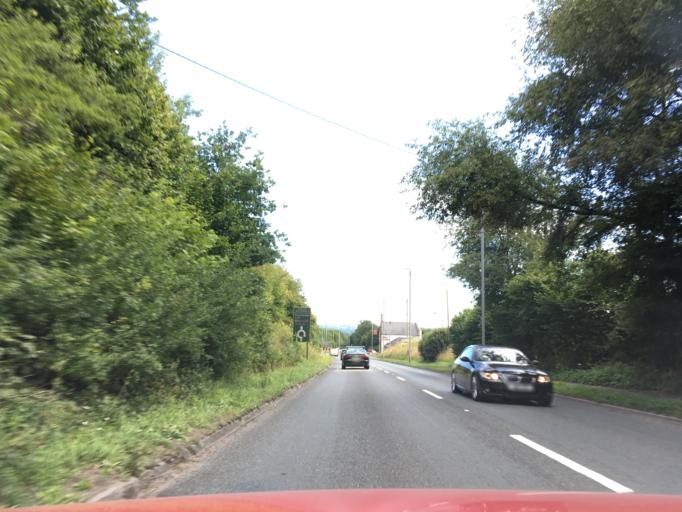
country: GB
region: England
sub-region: Somerset
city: Yeovil
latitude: 50.9243
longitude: -2.6360
